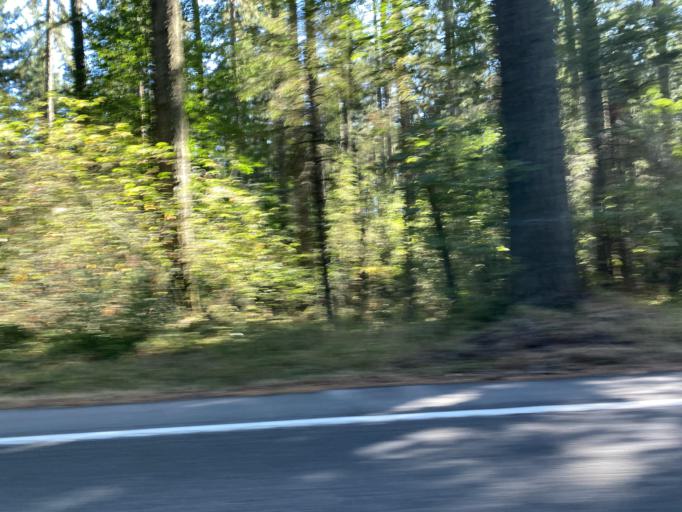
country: US
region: Washington
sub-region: Thurston County
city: Rainier
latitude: 46.9246
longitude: -122.7498
